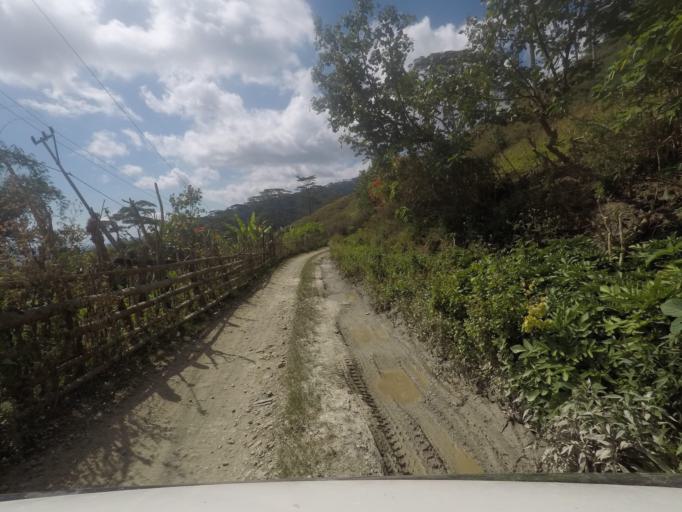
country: TL
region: Ermera
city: Gleno
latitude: -8.7511
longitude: 125.3256
